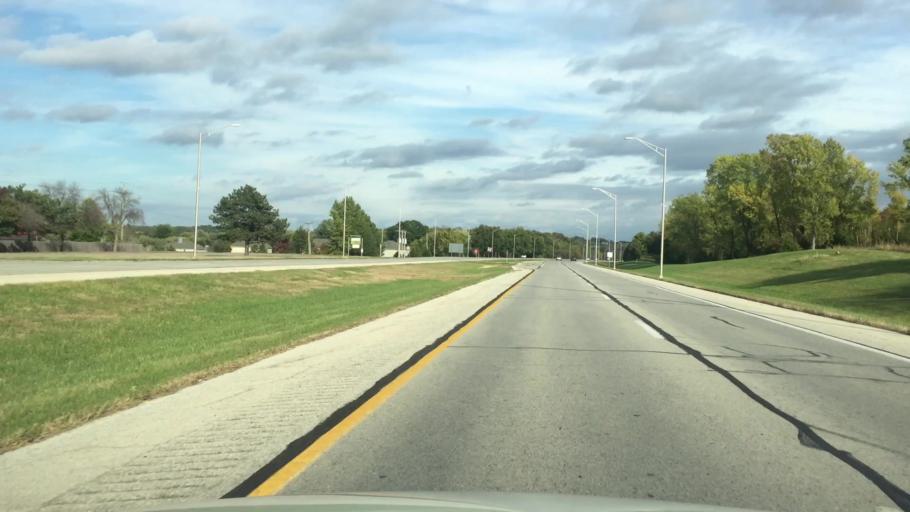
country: US
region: Kansas
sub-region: Wyandotte County
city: Edwardsville
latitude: 39.0087
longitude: -94.8349
